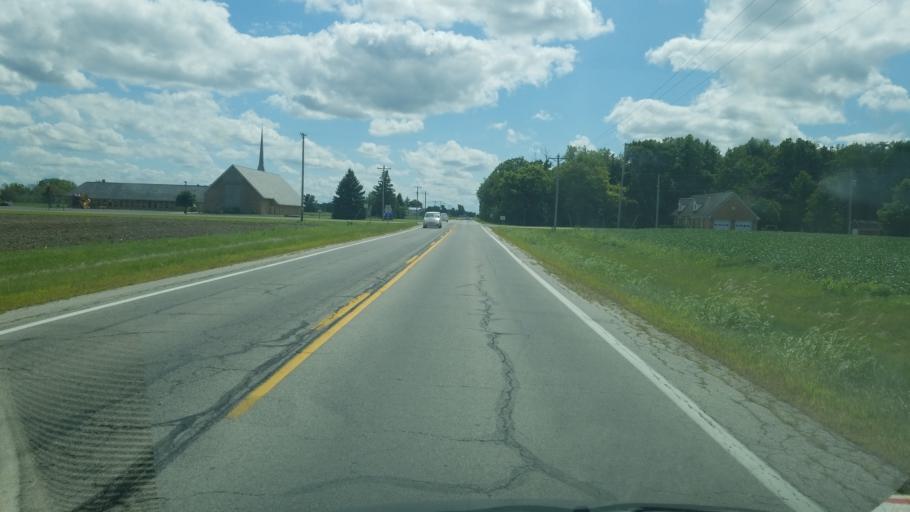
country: US
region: Ohio
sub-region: Henry County
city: Holgate
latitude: 41.2984
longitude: -84.1176
